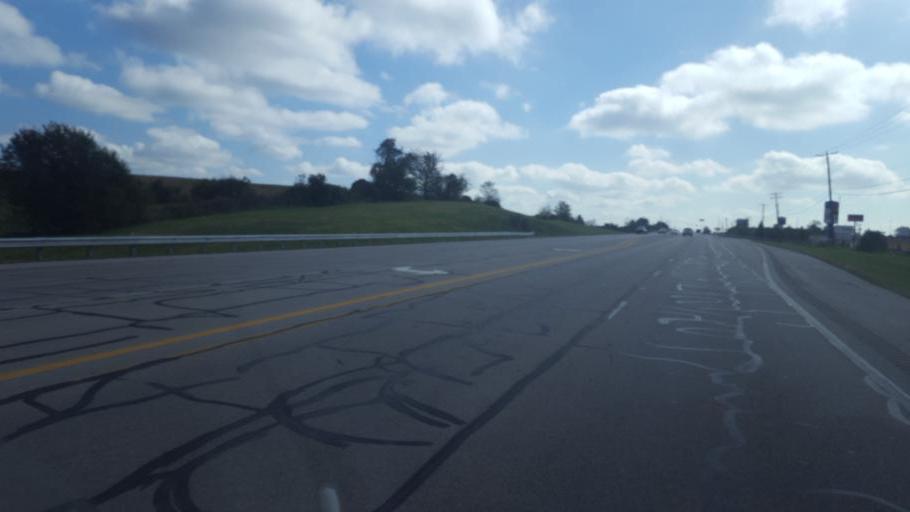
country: US
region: Ohio
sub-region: Brown County
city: Aberdeen
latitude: 38.6224
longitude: -83.7851
